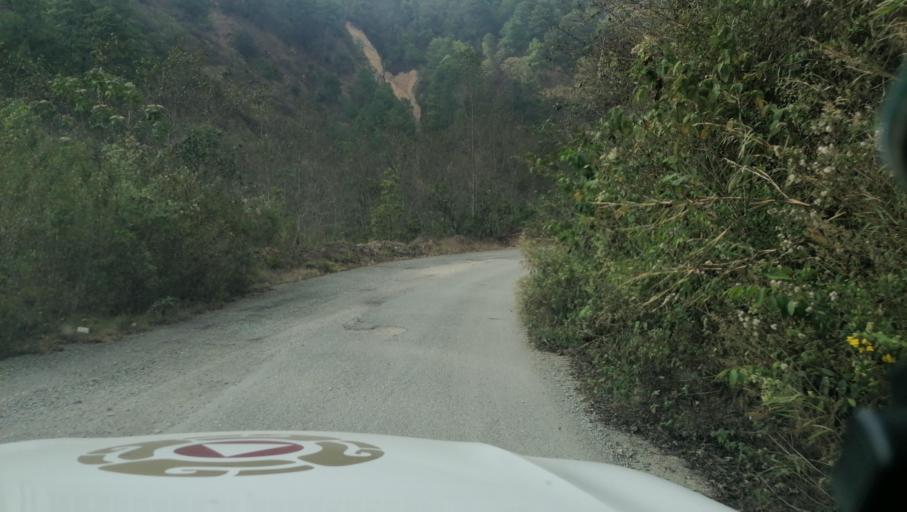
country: GT
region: San Marcos
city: Tacana
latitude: 15.2258
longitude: -92.1932
